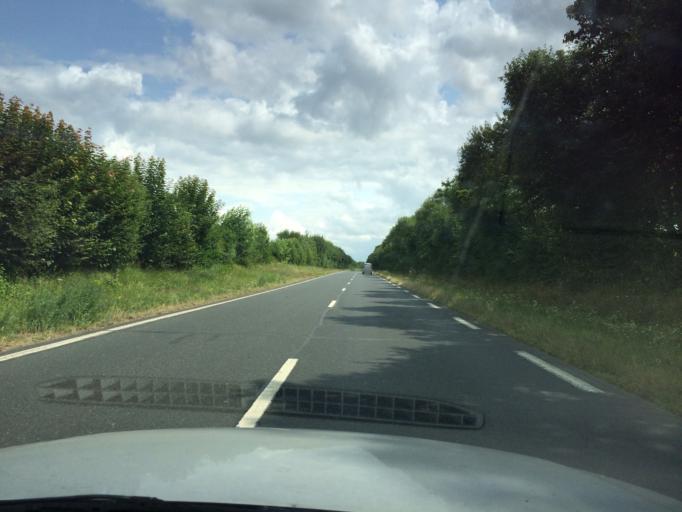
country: FR
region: Lower Normandy
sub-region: Departement du Calvados
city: Le Molay-Littry
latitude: 49.3306
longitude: -0.8932
